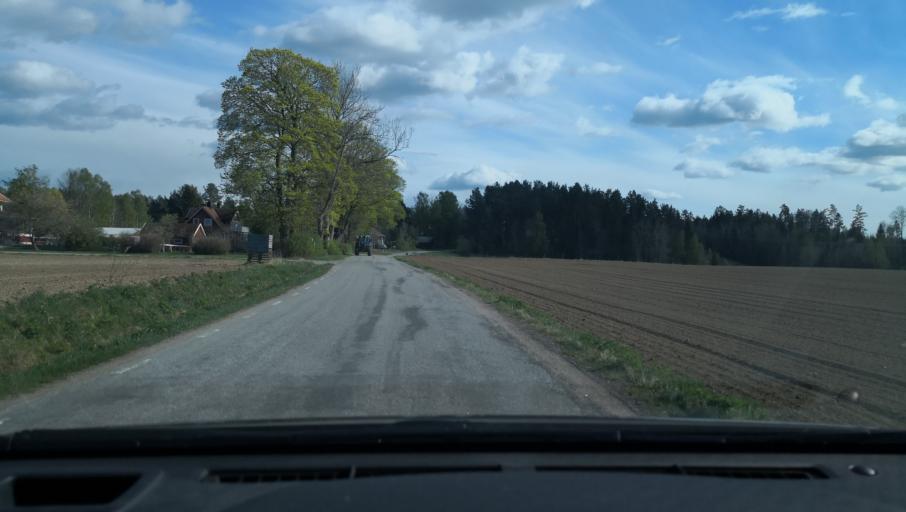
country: SE
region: OErebro
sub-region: Askersunds Kommun
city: Asbro
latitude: 58.9729
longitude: 15.0675
